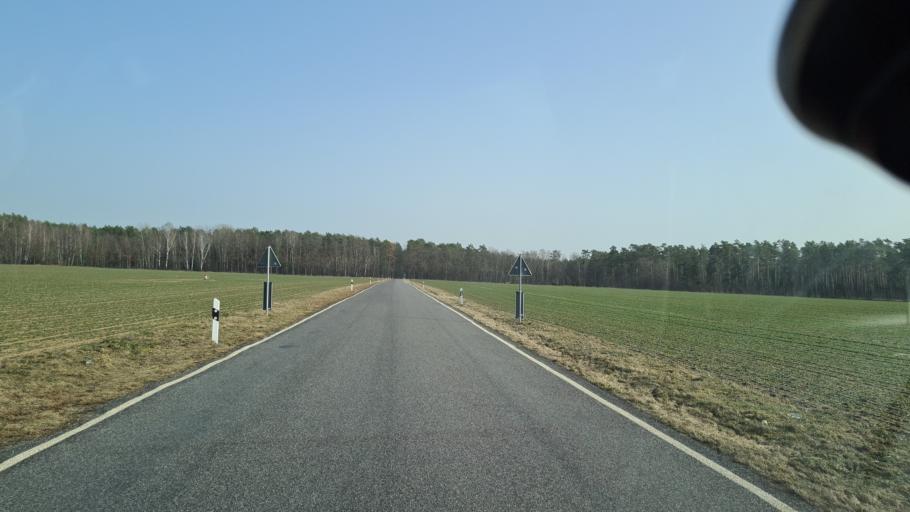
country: DE
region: Brandenburg
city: Cottbus
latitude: 51.6980
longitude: 14.4021
